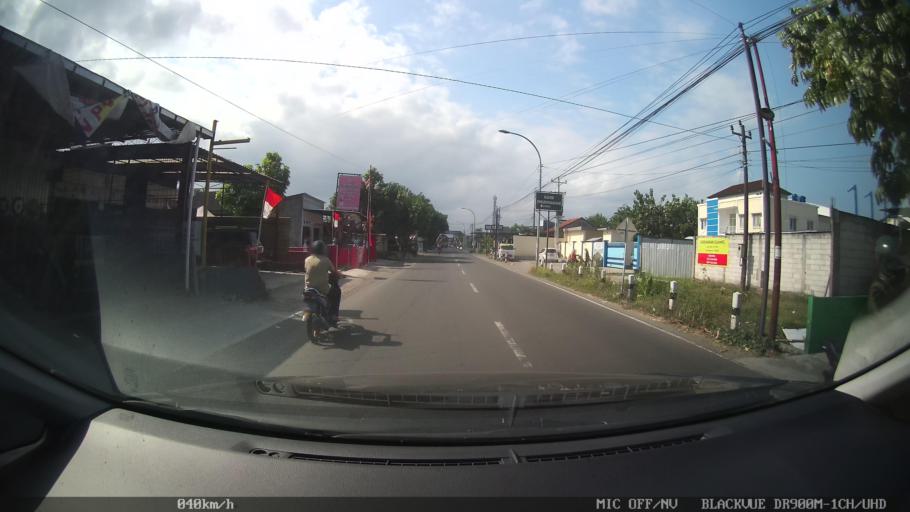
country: ID
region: Daerah Istimewa Yogyakarta
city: Sewon
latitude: -7.8573
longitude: 110.3899
